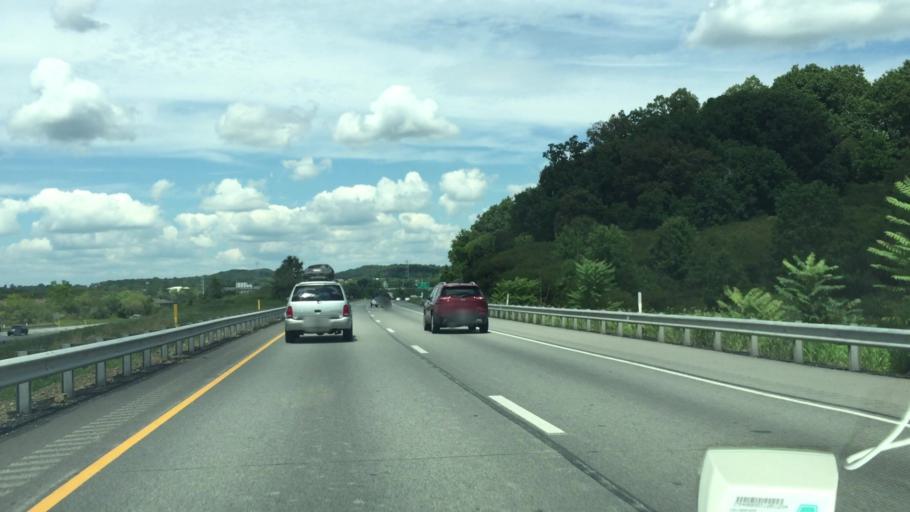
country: US
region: Pennsylvania
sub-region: Butler County
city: Cranberry Township
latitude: 40.6956
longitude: -80.0994
